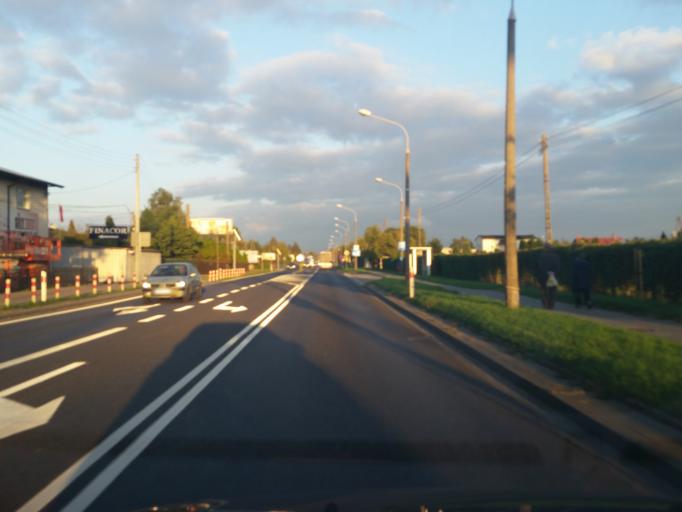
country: PL
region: Masovian Voivodeship
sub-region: Powiat warszawski zachodni
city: Ozarow Mazowiecki
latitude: 52.2109
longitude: 20.7776
